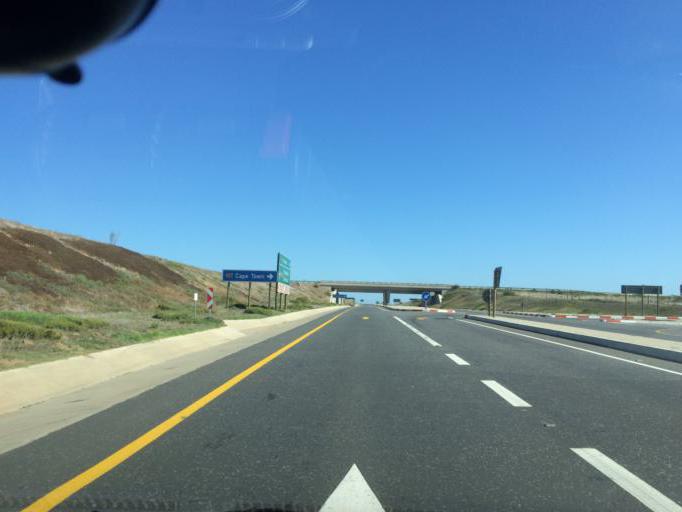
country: ZA
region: Western Cape
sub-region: City of Cape Town
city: Atlantis
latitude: -33.6640
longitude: 18.5613
